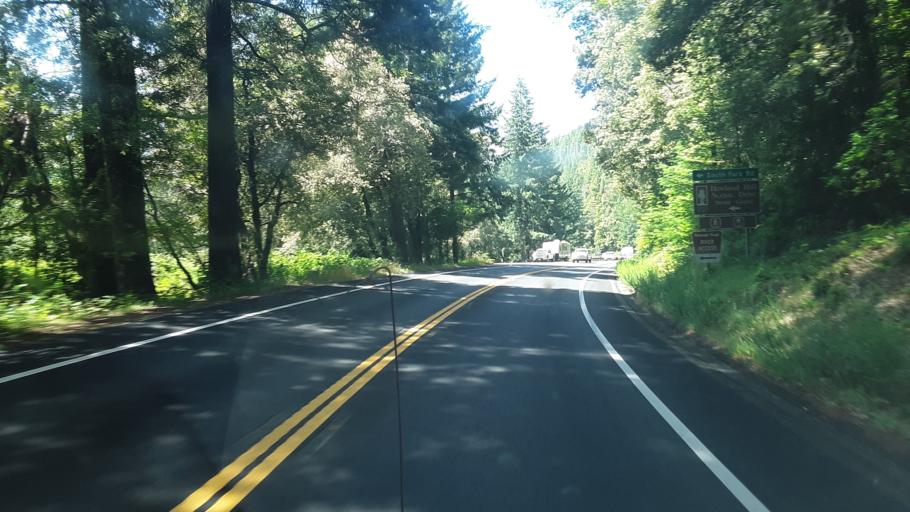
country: US
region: California
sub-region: Del Norte County
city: Bertsch-Oceanview
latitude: 41.8028
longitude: -124.0531
